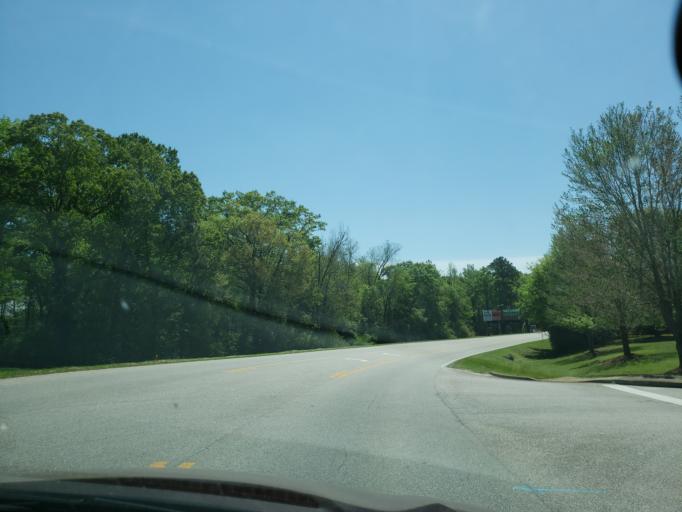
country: US
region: Alabama
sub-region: Lee County
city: Auburn
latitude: 32.6567
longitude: -85.5167
